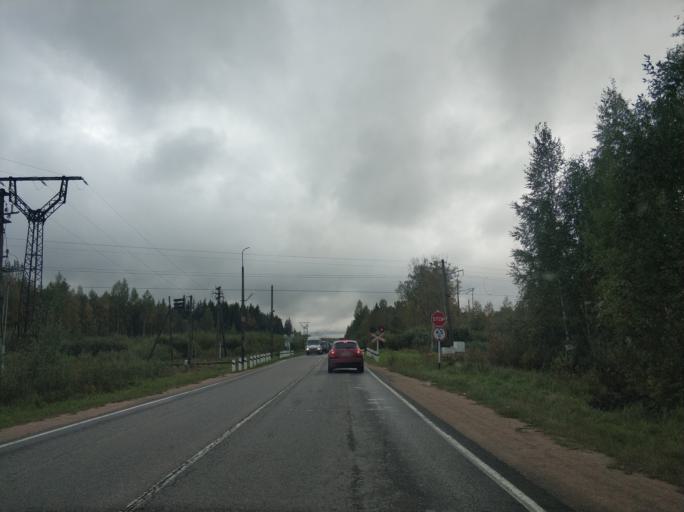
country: RU
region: Leningrad
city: Borisova Griva
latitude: 60.0957
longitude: 30.9531
